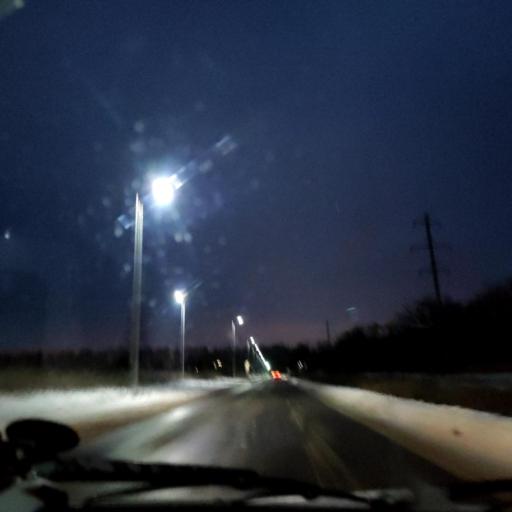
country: RU
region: Voronezj
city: Podgornoye
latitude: 51.7887
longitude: 39.1870
